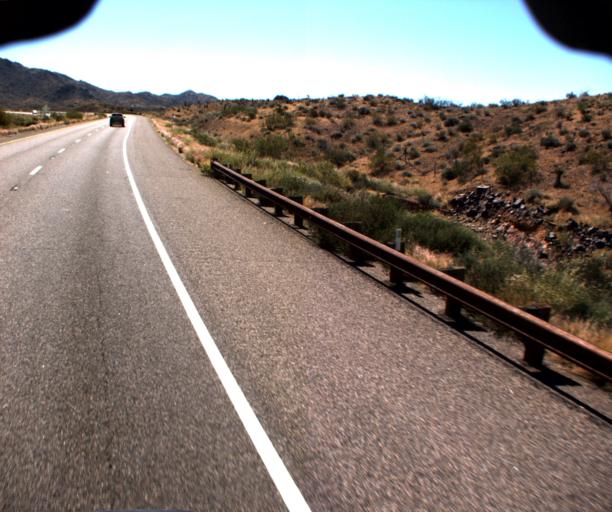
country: US
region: Nevada
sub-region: Clark County
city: Laughlin
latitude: 35.1963
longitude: -114.4144
